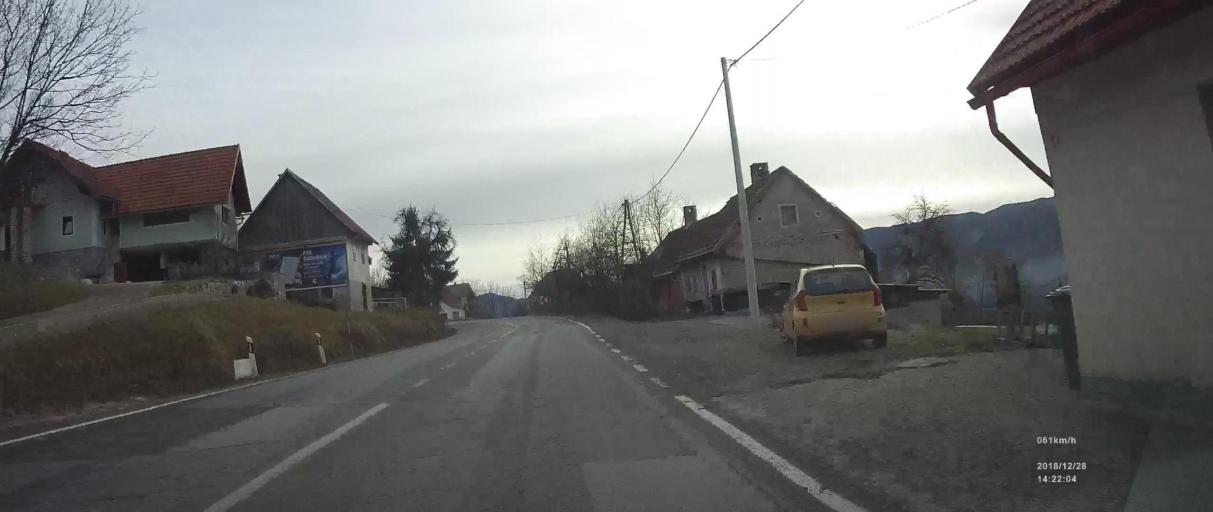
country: HR
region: Primorsko-Goranska
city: Vrbovsko
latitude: 45.3884
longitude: 15.0854
